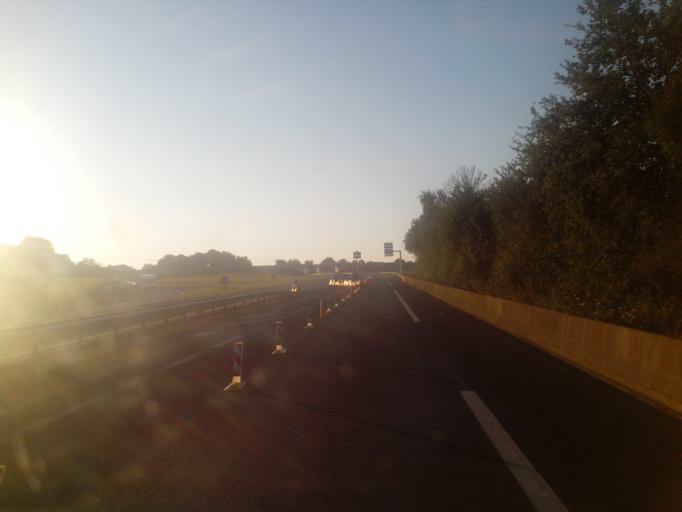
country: FR
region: Brittany
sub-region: Departement des Cotes-d'Armor
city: Loudeac
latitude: 48.1896
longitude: -2.7482
